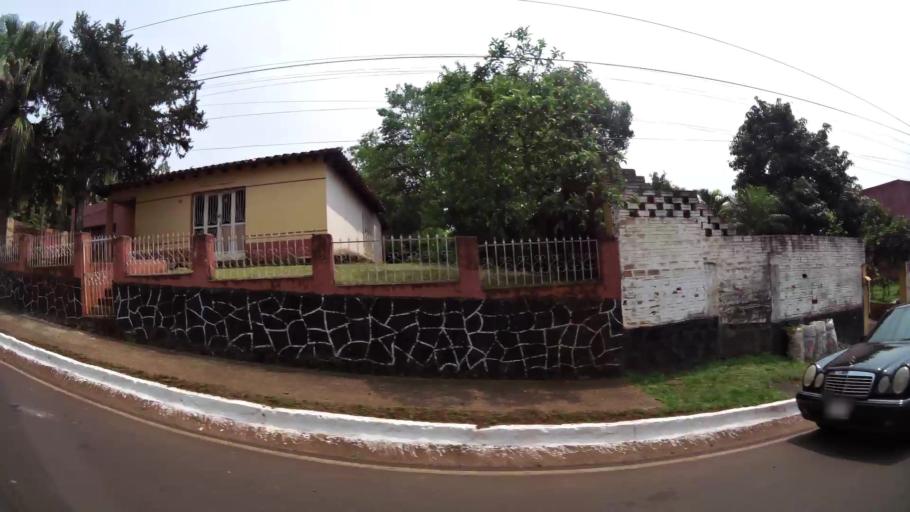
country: BR
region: Parana
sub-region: Foz Do Iguacu
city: Foz do Iguacu
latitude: -25.5573
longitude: -54.6009
